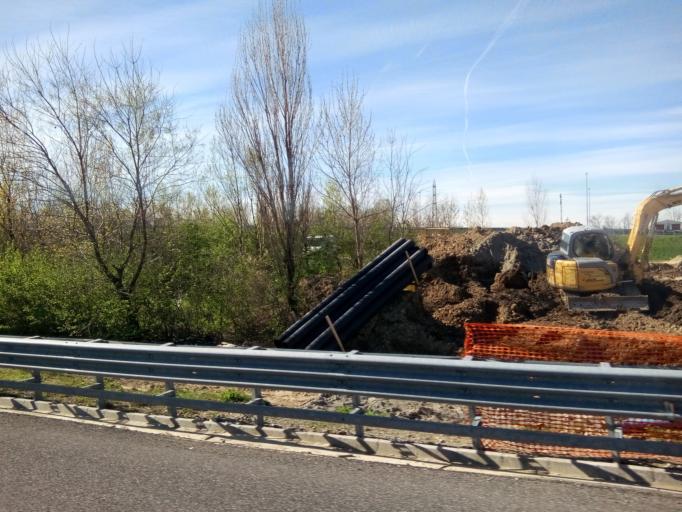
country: IT
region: Lombardy
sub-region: Citta metropolitana di Milano
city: Pero
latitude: 45.5306
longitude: 9.0924
